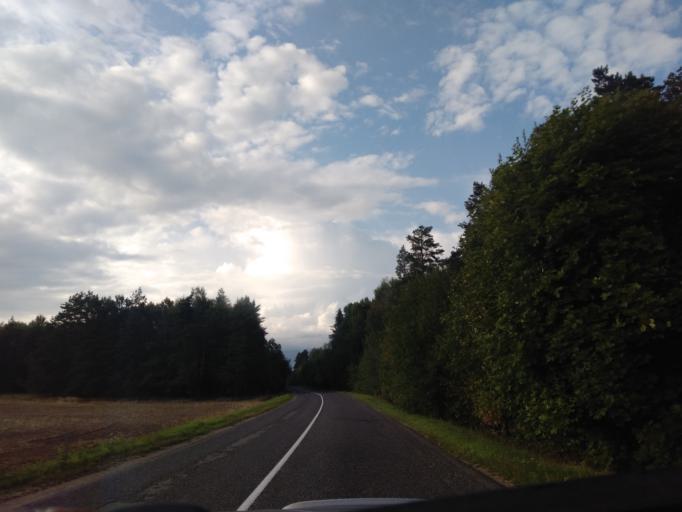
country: BY
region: Minsk
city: Kapyl'
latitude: 53.2921
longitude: 27.0808
